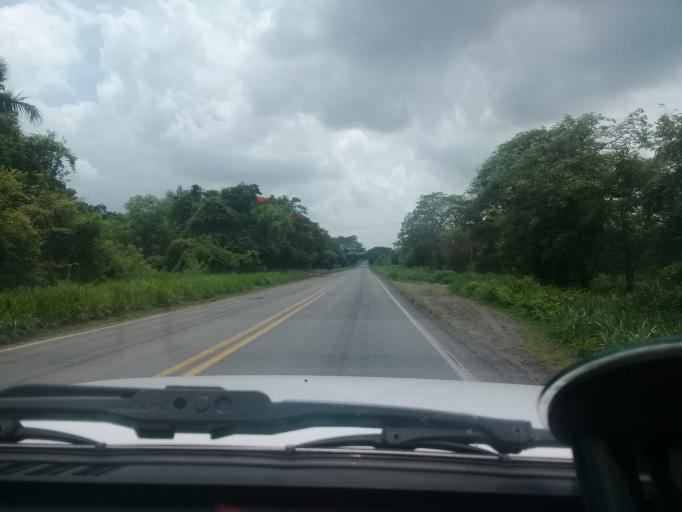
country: MX
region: Veracruz
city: Paso de Ovejas
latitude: 19.2912
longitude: -96.4515
